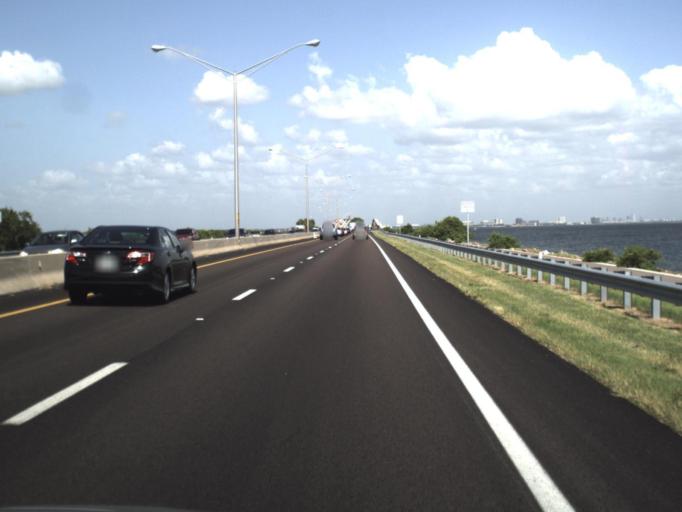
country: US
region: Florida
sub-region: Pinellas County
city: Safety Harbor
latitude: 27.9683
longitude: -82.6381
